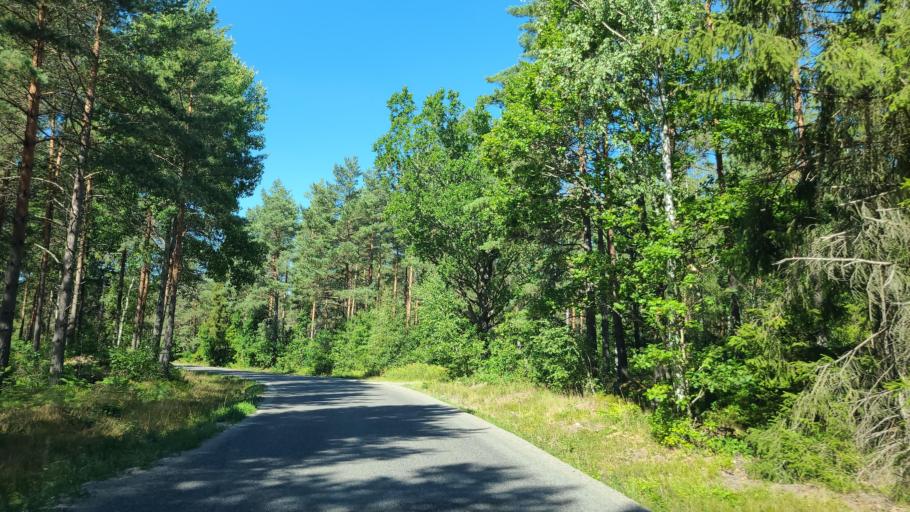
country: SE
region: Kalmar
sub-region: Kalmar Kommun
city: Ljungbyholm
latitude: 56.5715
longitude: 16.0409
